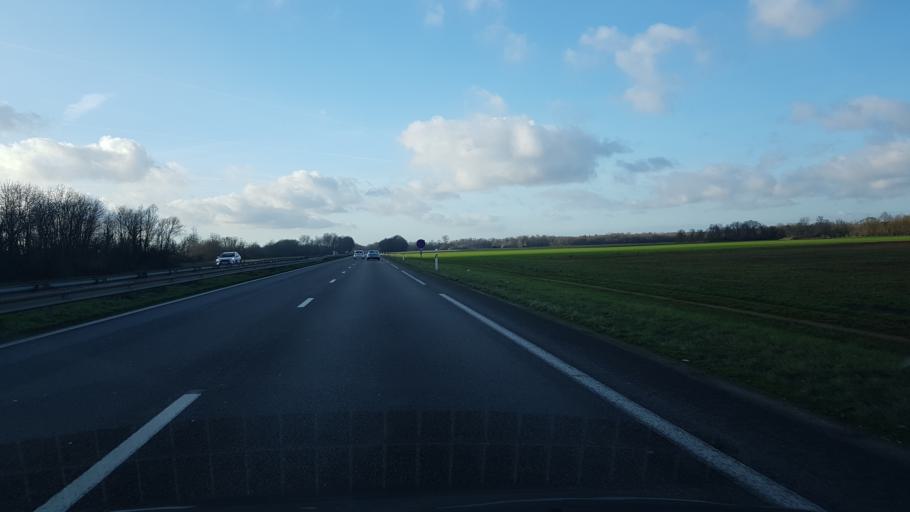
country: FR
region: Champagne-Ardenne
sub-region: Departement de la Haute-Marne
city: Villiers-en-Lieu
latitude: 48.6430
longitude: 4.8923
